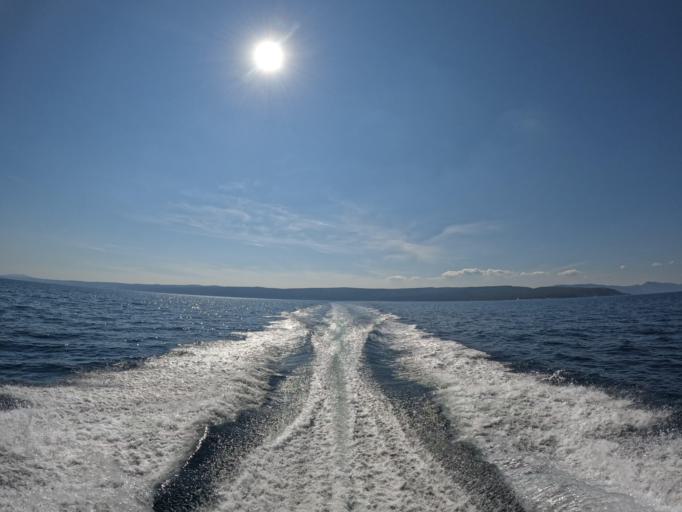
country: HR
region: Primorsko-Goranska
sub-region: Grad Krk
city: Krk
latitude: 44.9470
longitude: 14.5246
